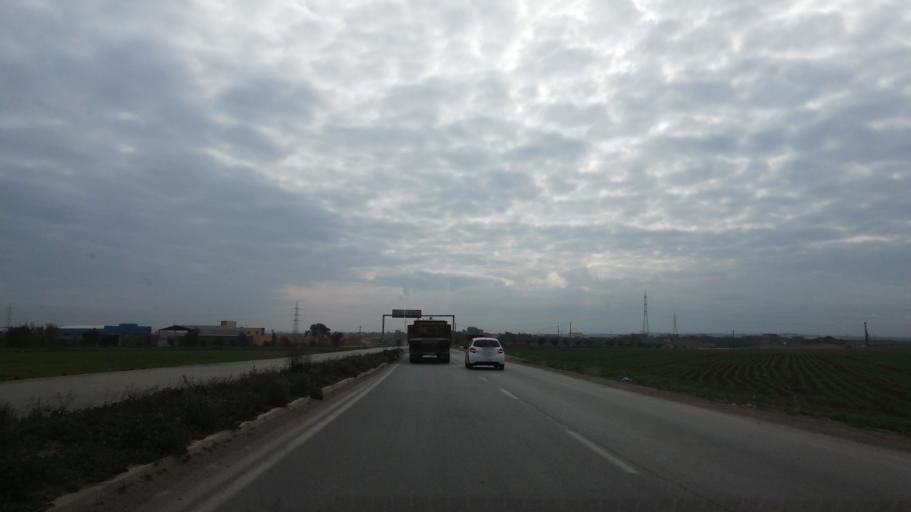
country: DZ
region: Oran
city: Ain el Bya
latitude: 35.7954
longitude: -0.3434
